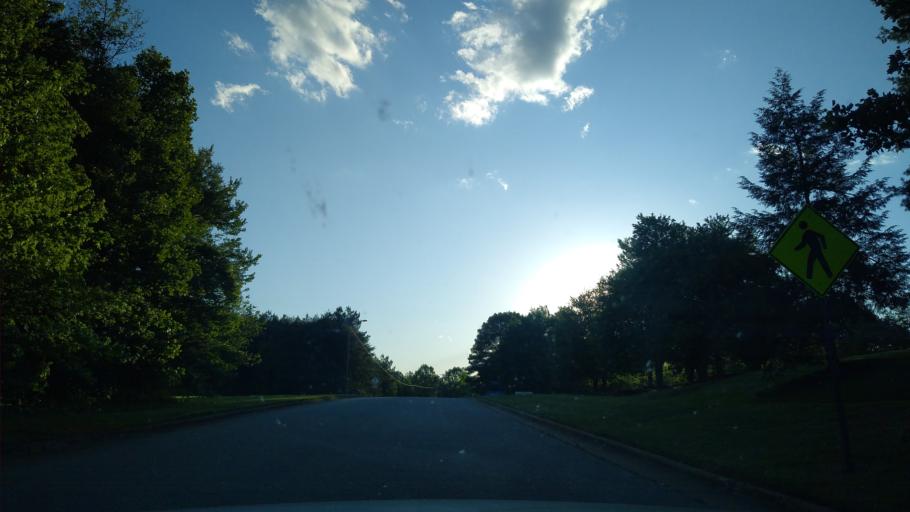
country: US
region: North Carolina
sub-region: Guilford County
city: Oak Ridge
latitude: 36.0864
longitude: -79.9664
